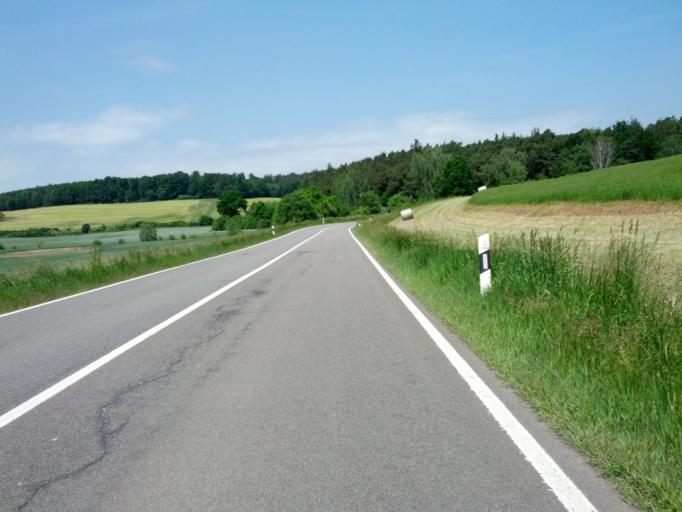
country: DE
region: Thuringia
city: Urnshausen
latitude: 50.7424
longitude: 10.1719
